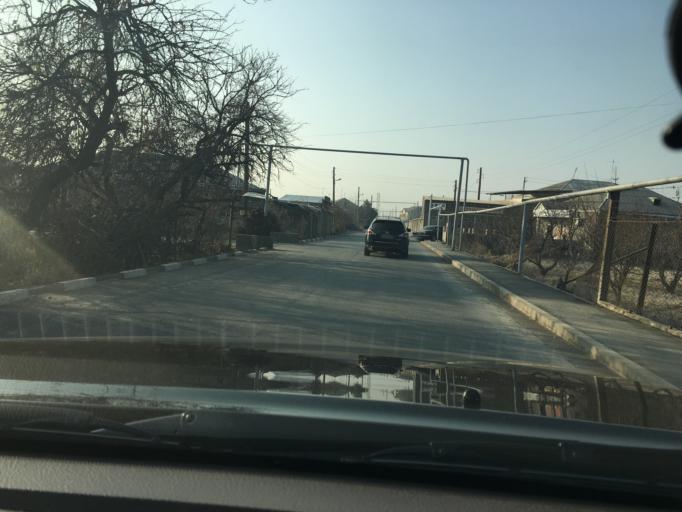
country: AM
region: Armavir
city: Janfida
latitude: 40.0504
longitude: 44.0321
